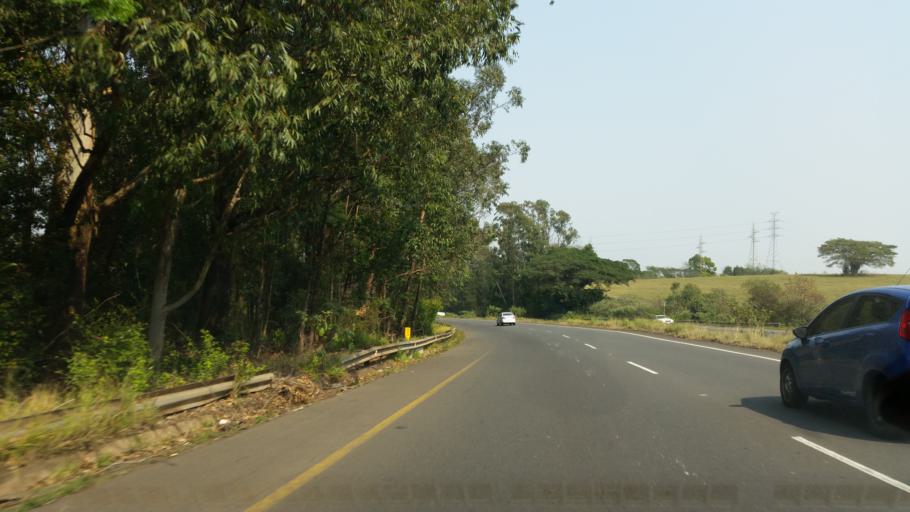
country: ZA
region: KwaZulu-Natal
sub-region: eThekwini Metropolitan Municipality
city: Mpumalanga
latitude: -29.7991
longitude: 30.7588
